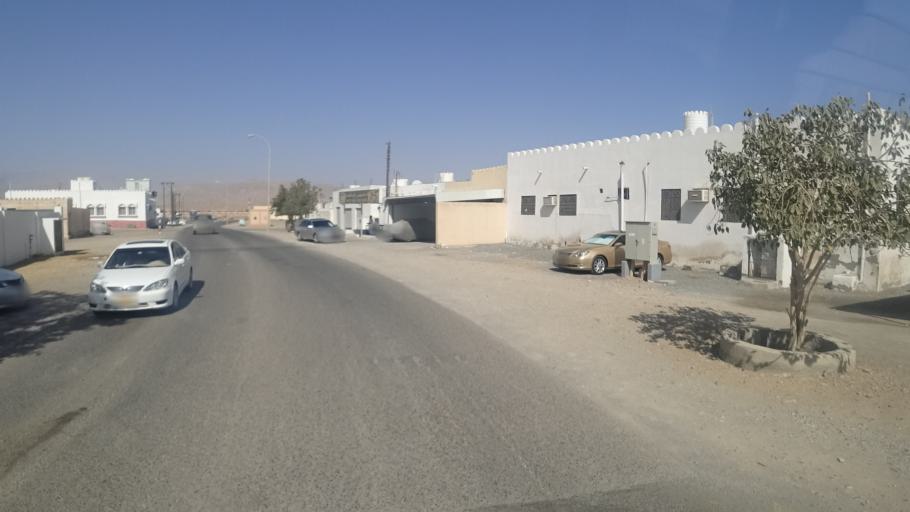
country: OM
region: Ash Sharqiyah
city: Sur
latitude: 22.5406
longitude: 59.4850
